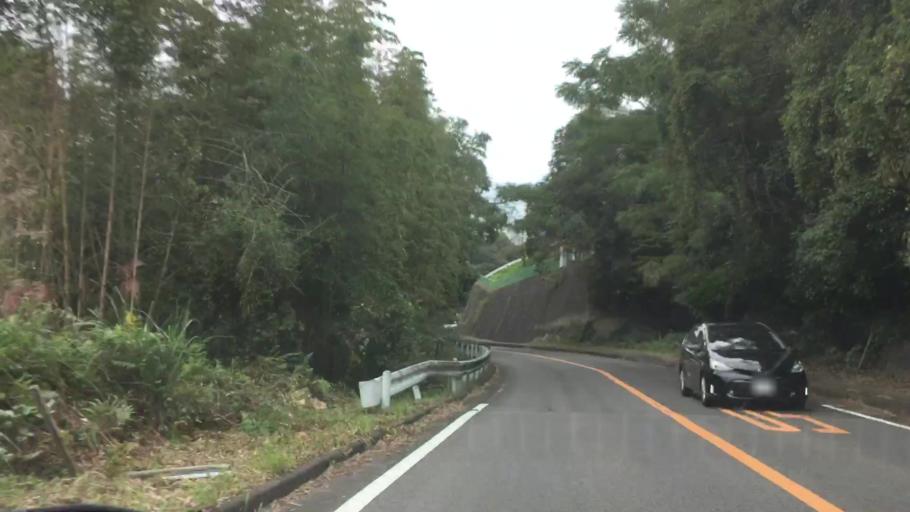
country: JP
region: Nagasaki
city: Sasebo
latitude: 32.9976
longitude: 129.7259
